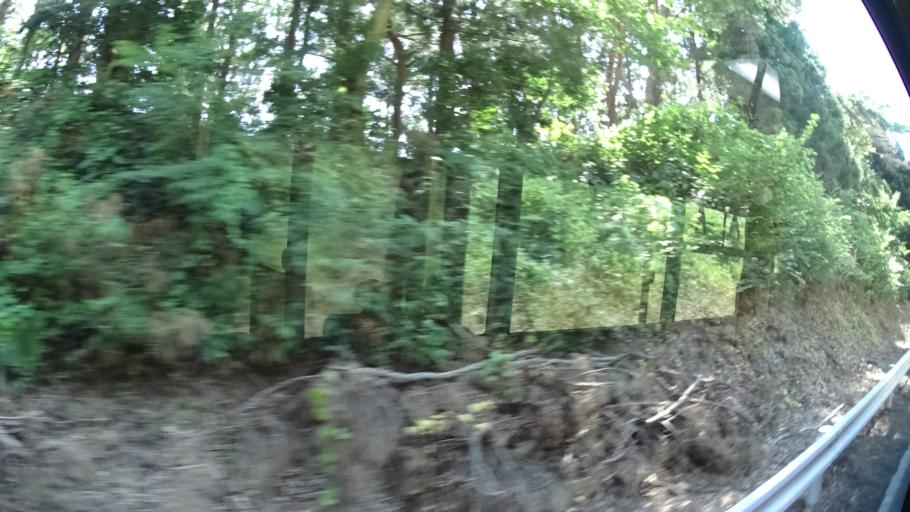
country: JP
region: Iwate
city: Ofunato
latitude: 38.9947
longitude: 141.7102
